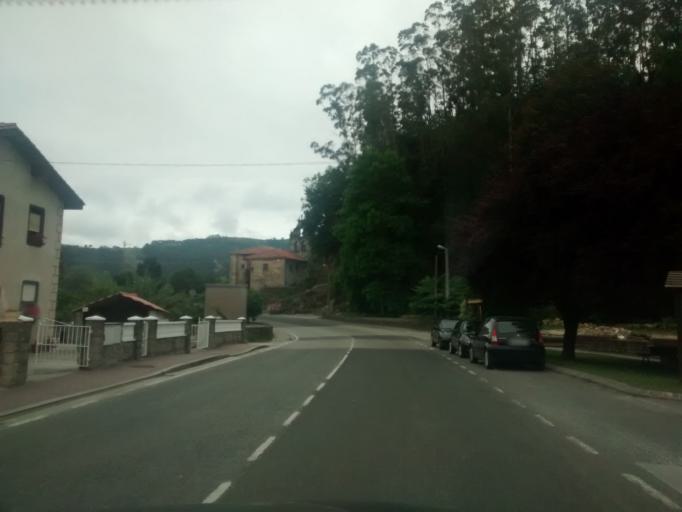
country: ES
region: Cantabria
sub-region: Provincia de Cantabria
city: Luzmela
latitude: 43.3205
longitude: -4.1911
